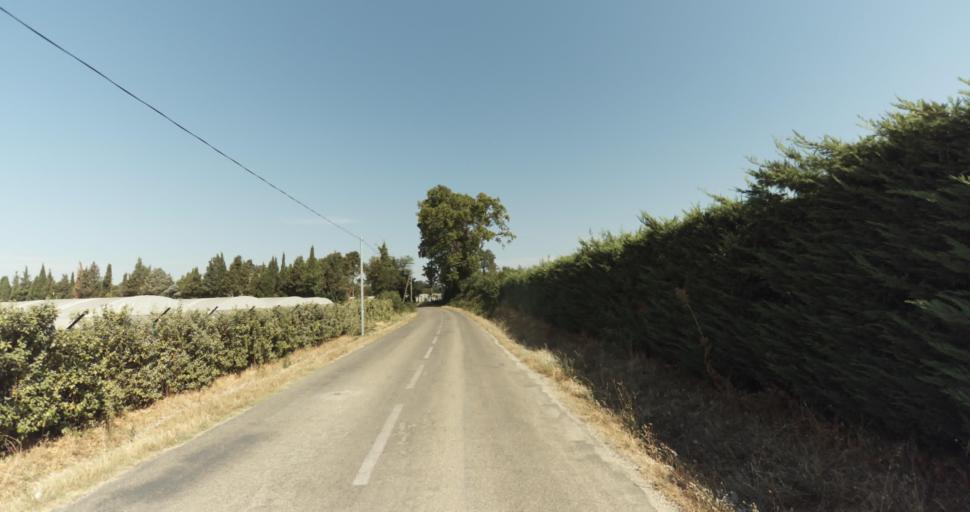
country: FR
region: Provence-Alpes-Cote d'Azur
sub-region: Departement du Vaucluse
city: Monteux
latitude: 44.0273
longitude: 5.0148
